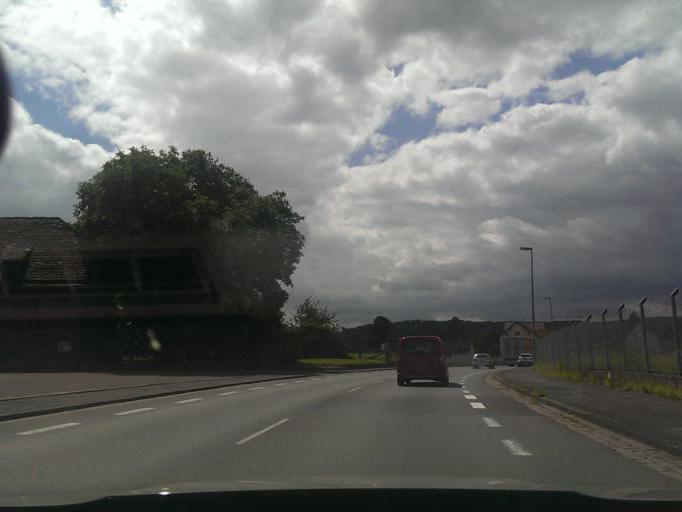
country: DE
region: Lower Saxony
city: Negenborn
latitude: 51.8901
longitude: 9.5717
